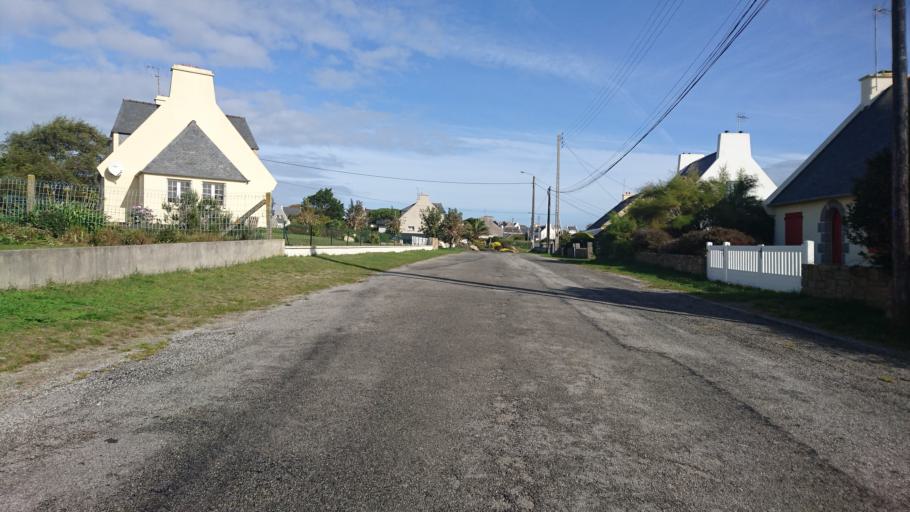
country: FR
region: Brittany
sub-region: Departement du Finistere
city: Lampaul-Plouarzel
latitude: 48.4452
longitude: -4.7701
